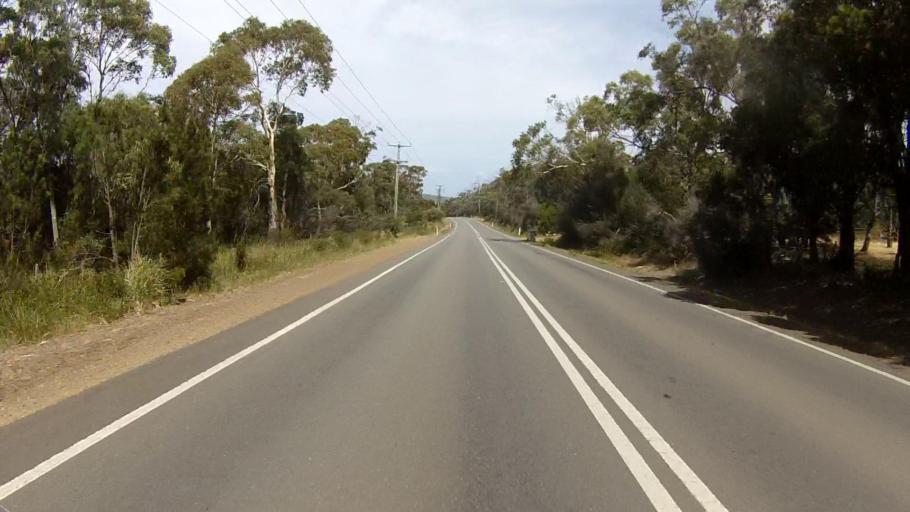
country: AU
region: Tasmania
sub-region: Clarence
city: Sandford
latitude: -43.0084
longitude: 147.4930
